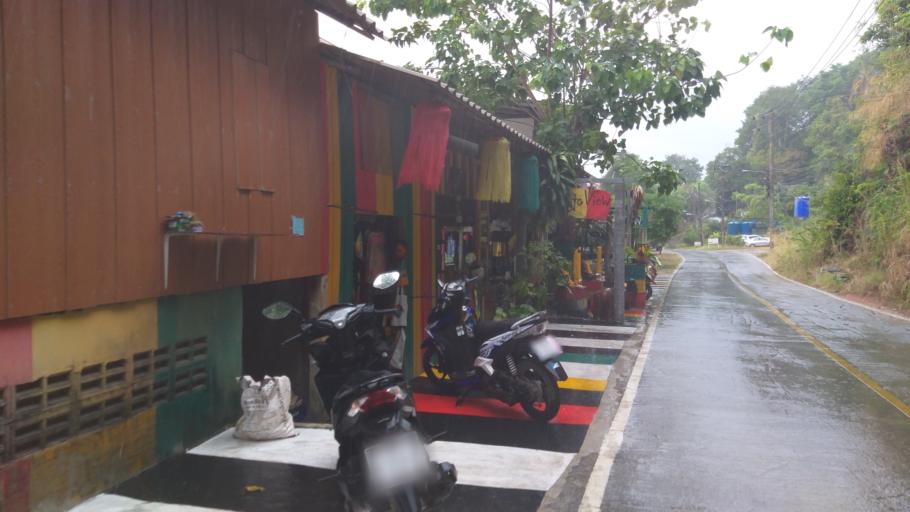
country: TH
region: Trat
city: Ko Chang Tai
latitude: 11.9751
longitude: 102.3178
